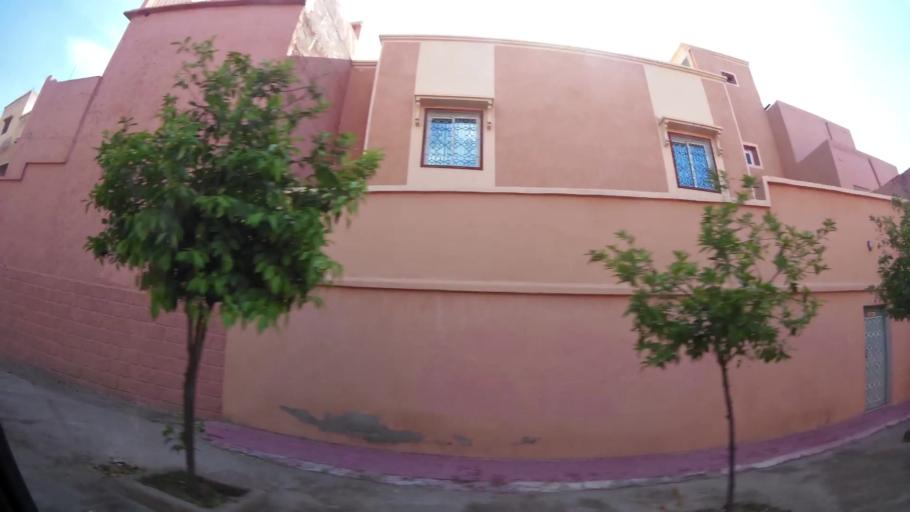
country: MA
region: Marrakech-Tensift-Al Haouz
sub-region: Marrakech
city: Marrakesh
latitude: 31.6459
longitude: -8.0055
